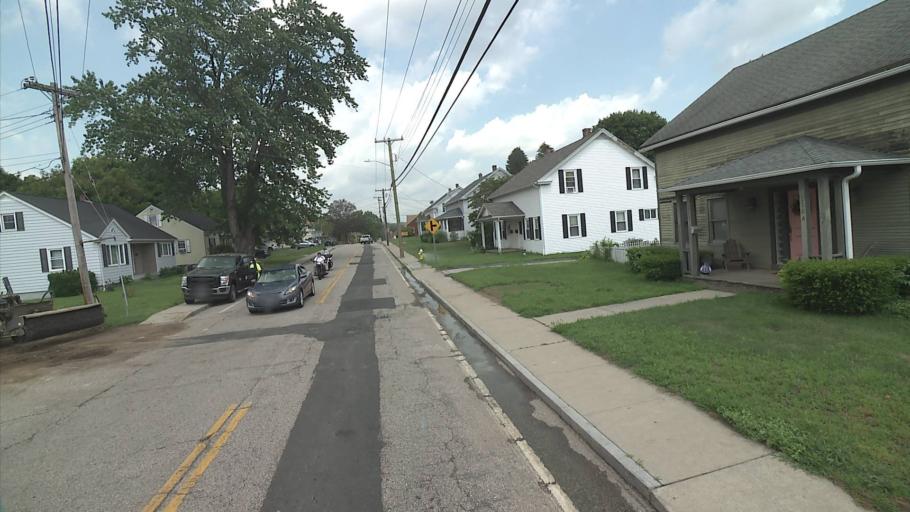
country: US
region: Connecticut
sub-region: New London County
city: Jewett City
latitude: 41.6011
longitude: -71.9814
